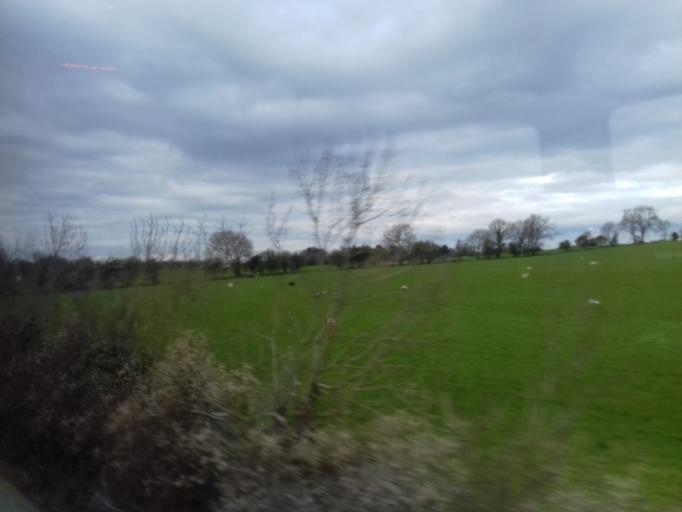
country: IE
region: Leinster
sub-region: An Longfort
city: Granard
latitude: 53.6690
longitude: -7.4943
